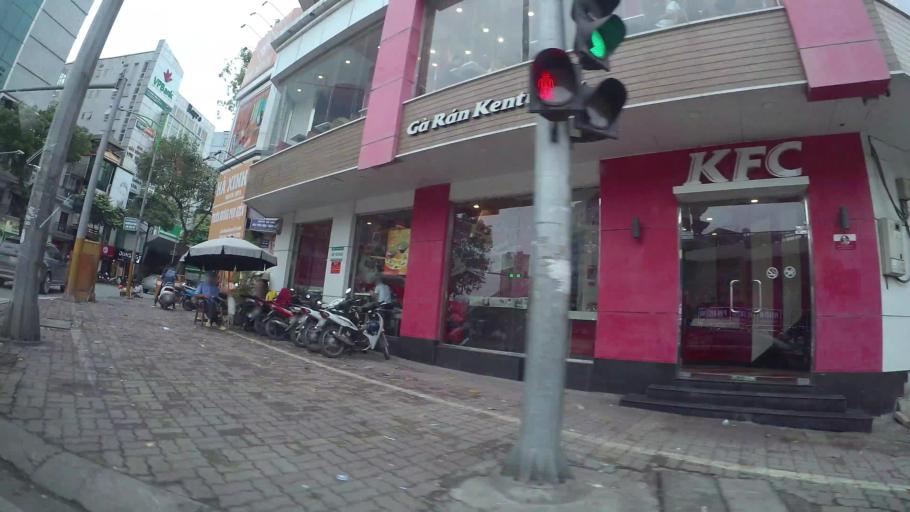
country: VN
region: Ha Noi
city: Hai BaTrung
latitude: 21.0089
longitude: 105.8518
